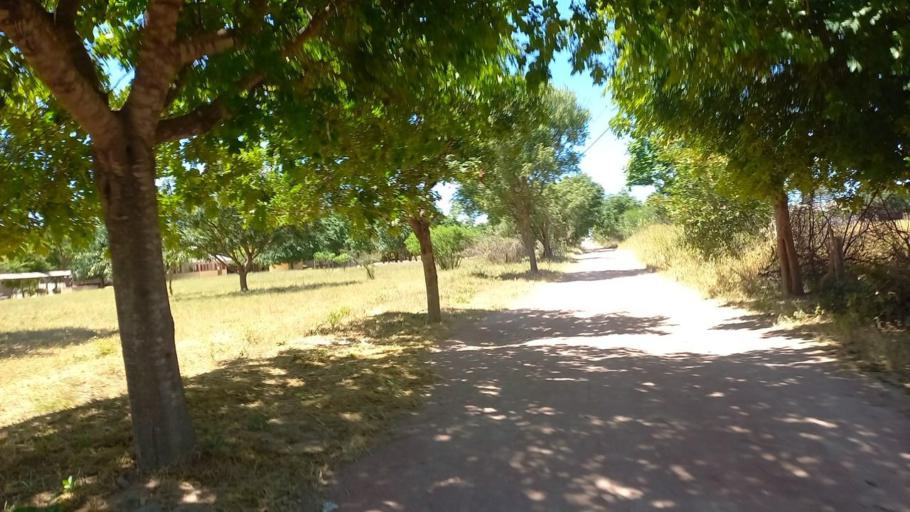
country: TZ
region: Dodoma
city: Dodoma
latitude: -6.1174
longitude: 35.7402
